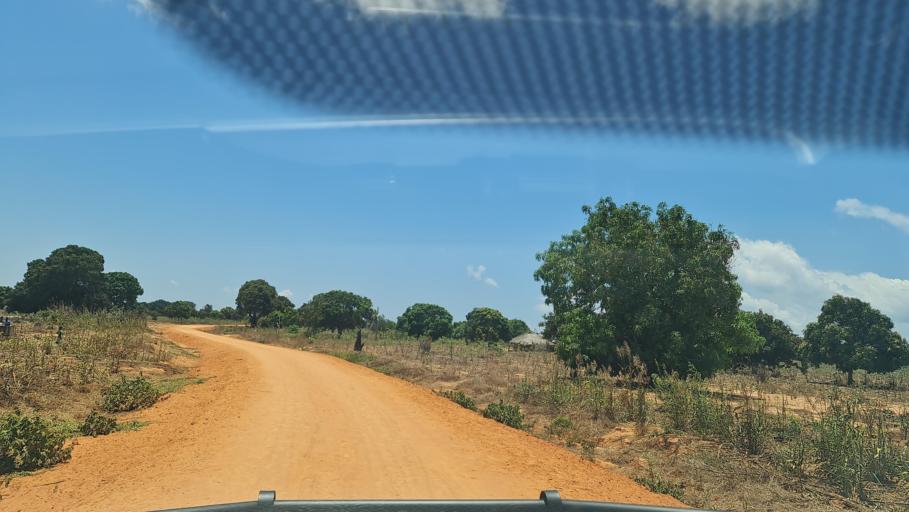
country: MZ
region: Nampula
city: Nacala
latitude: -14.2239
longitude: 40.6858
